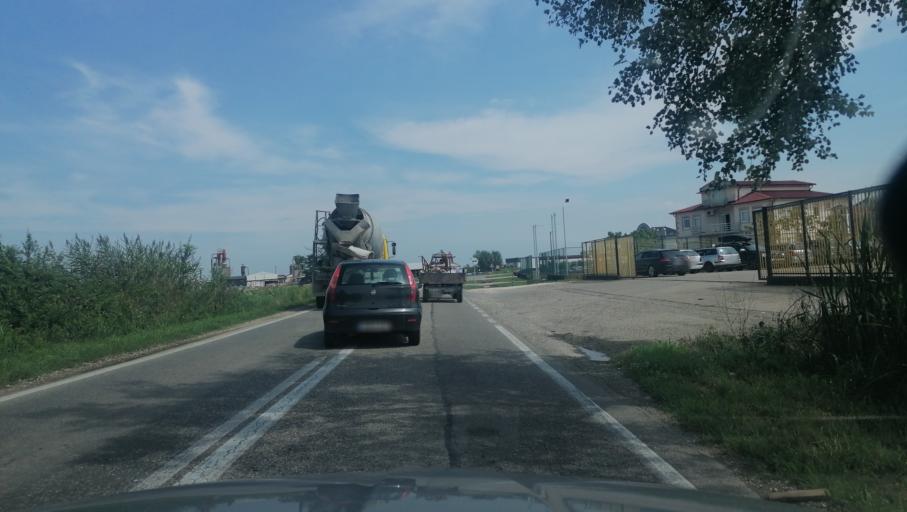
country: BA
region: Republika Srpska
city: Velika Obarska
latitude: 44.7696
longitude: 19.1457
